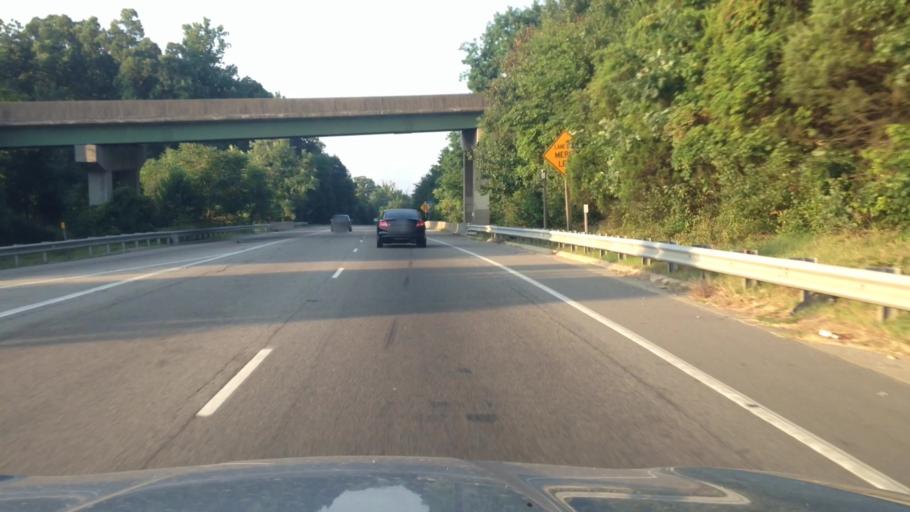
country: US
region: Virginia
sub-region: Prince William County
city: Woodbridge
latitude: 38.6769
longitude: -77.2336
